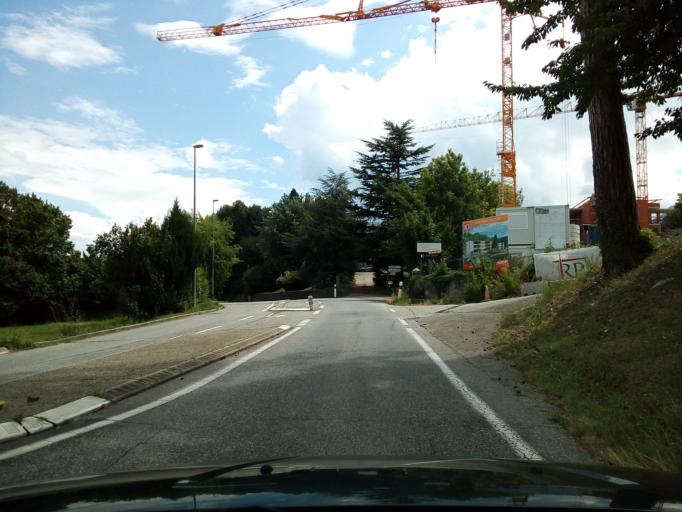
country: FR
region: Rhone-Alpes
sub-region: Departement de la Savoie
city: Saint-Baldoph
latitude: 45.5472
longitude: 5.9570
